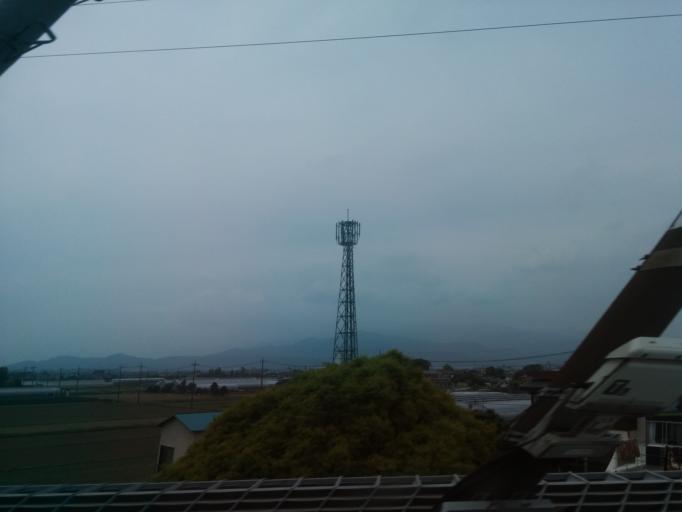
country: JP
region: Kanagawa
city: Isehara
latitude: 35.3539
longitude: 139.3185
